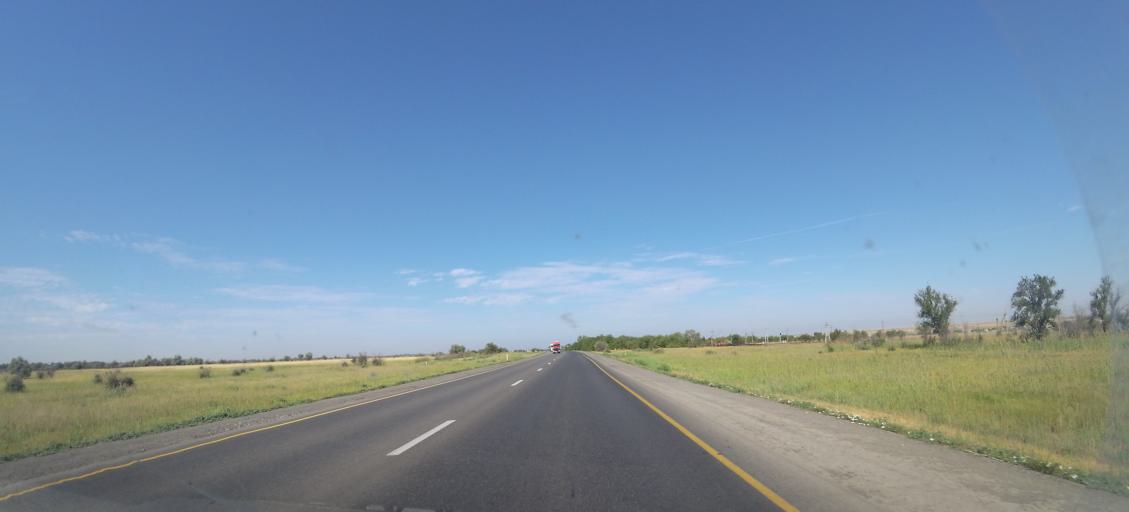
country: RU
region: Volgograd
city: Novyy Rogachik
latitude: 48.6858
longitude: 43.9424
